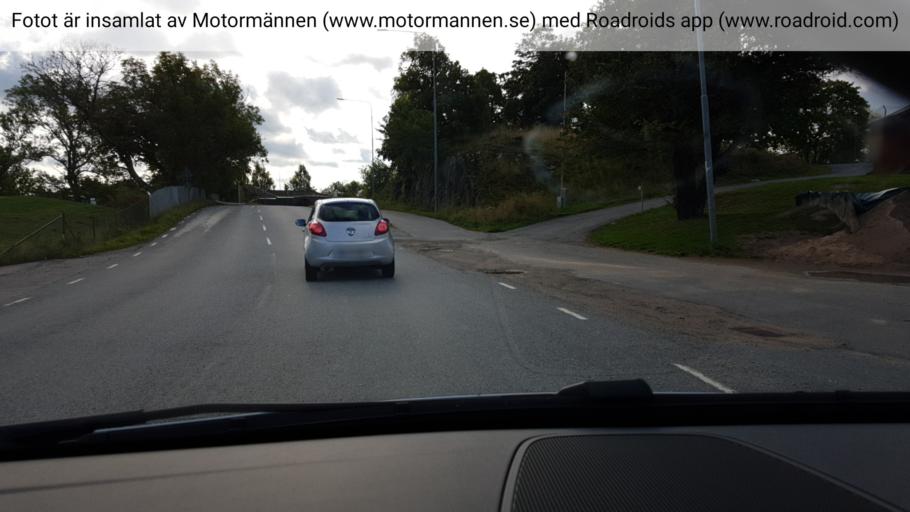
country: SE
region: Stockholm
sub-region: Lidingo
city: Lidingoe
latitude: 59.3777
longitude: 18.1274
